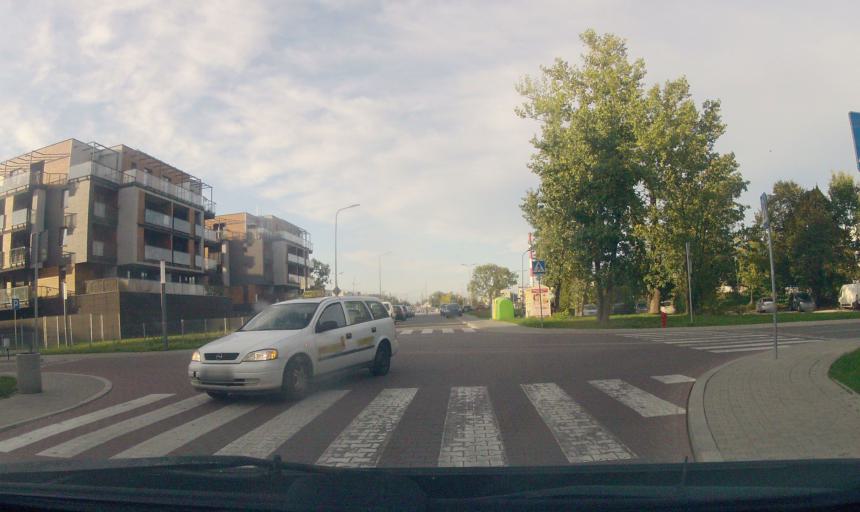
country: PL
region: Lesser Poland Voivodeship
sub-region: Krakow
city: Krakow
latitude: 50.0380
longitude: 20.0010
